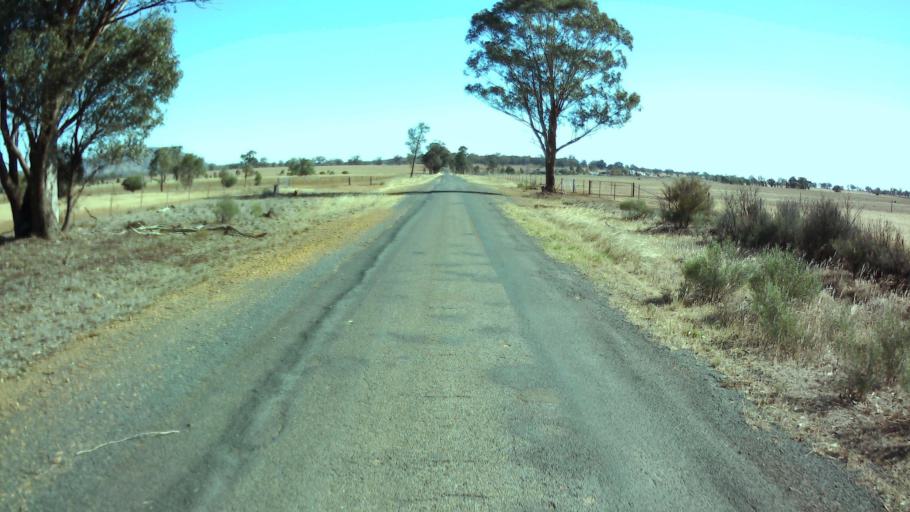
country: AU
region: New South Wales
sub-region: Weddin
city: Grenfell
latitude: -33.7998
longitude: 147.9560
